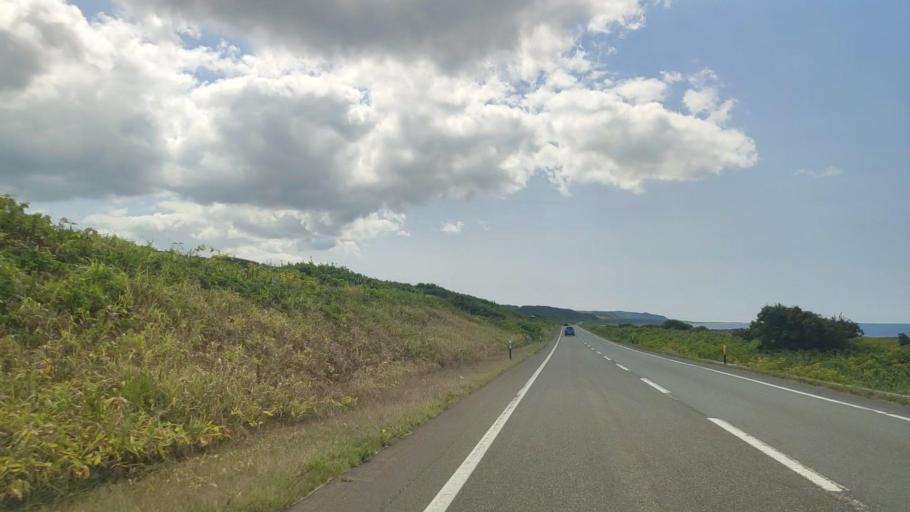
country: JP
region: Hokkaido
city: Wakkanai
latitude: 45.2852
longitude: 141.6192
